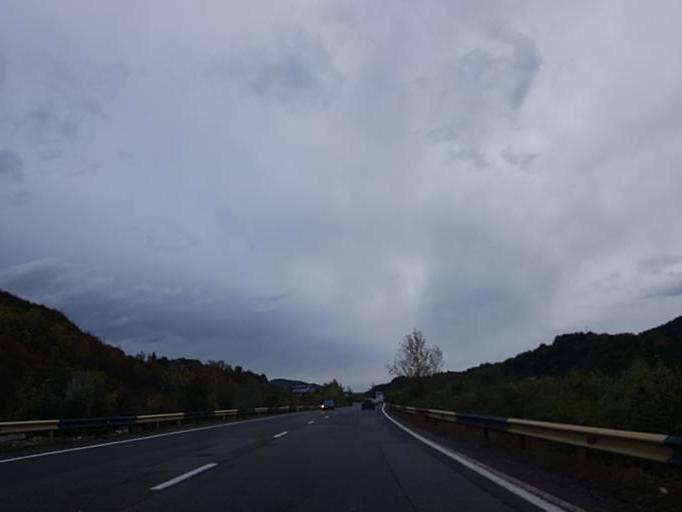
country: RO
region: Prahova
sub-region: Oras Breaza
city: Gura Beliei
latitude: 45.2214
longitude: 25.6448
